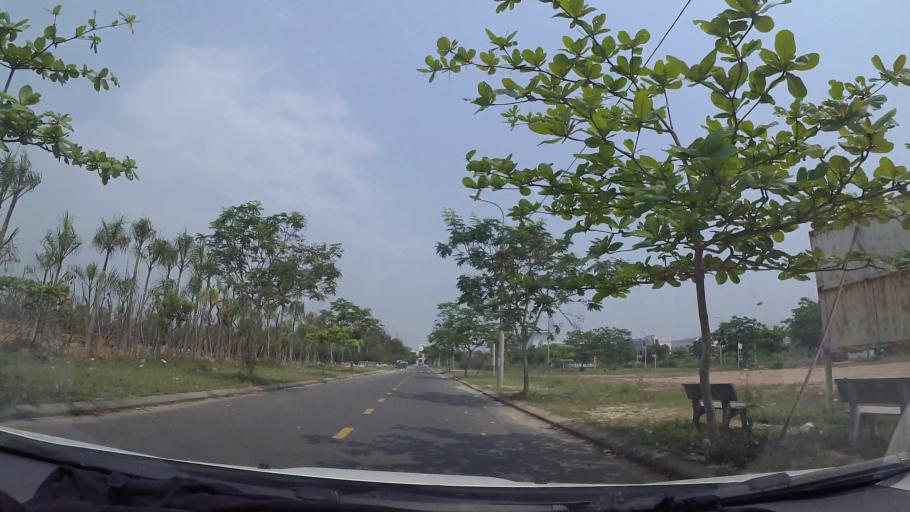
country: VN
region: Da Nang
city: Cam Le
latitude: 15.9957
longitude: 108.2105
